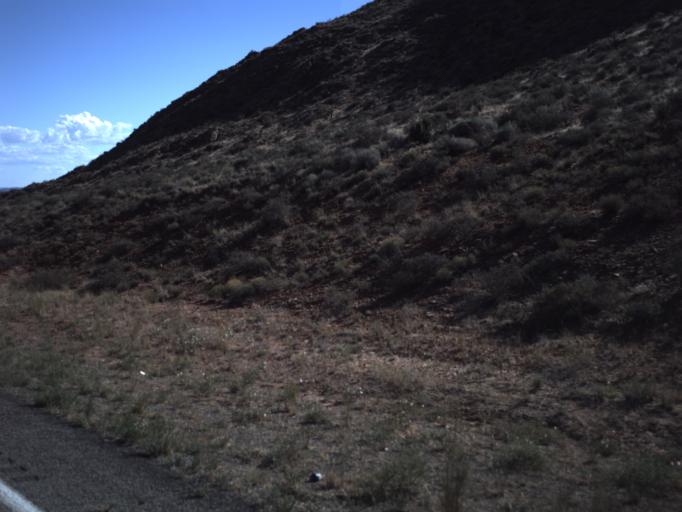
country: US
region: Utah
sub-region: Washington County
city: Toquerville
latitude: 37.2713
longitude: -113.2966
